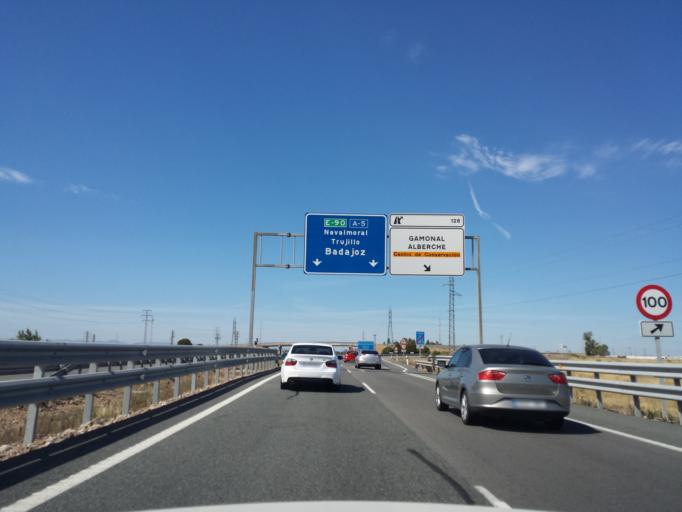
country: ES
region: Castille-La Mancha
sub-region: Province of Toledo
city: Velada
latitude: 39.9453
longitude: -4.9484
